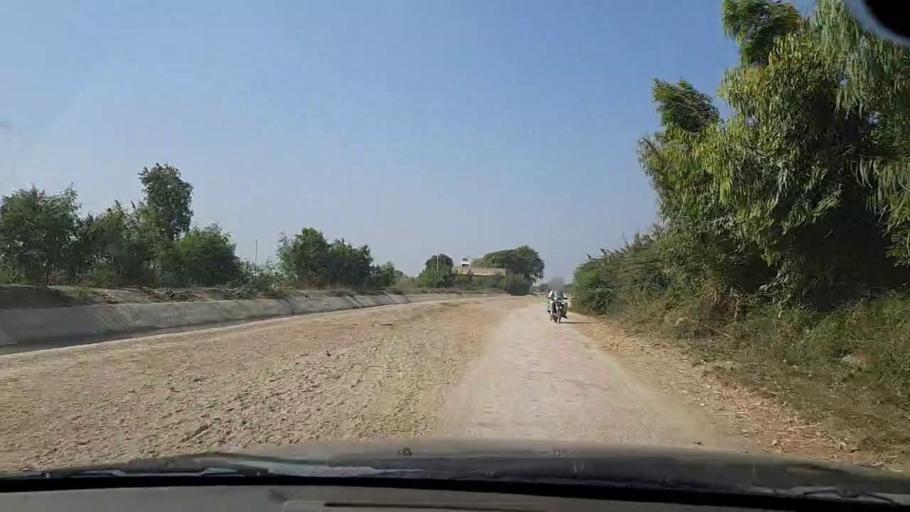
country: PK
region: Sindh
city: Chuhar Jamali
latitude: 24.4259
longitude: 67.8145
